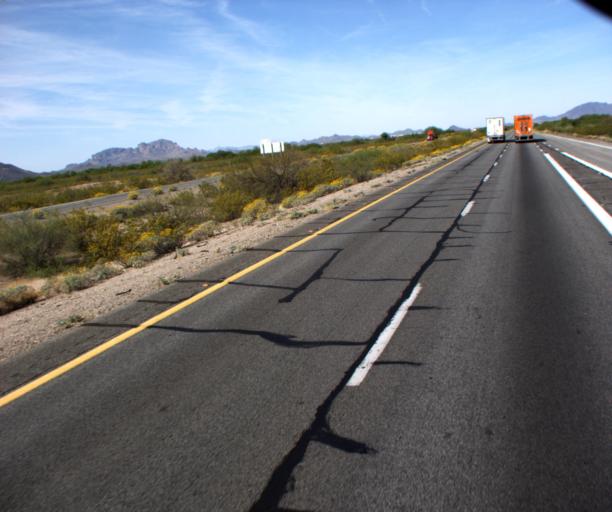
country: US
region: Arizona
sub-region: Maricopa County
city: Buckeye
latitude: 33.4836
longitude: -112.8743
